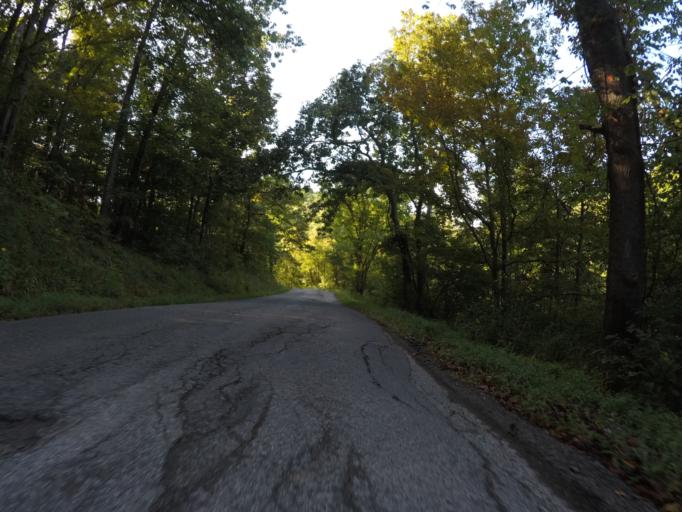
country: US
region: Kentucky
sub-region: Boyd County
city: Ashland
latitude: 38.5256
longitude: -82.5331
